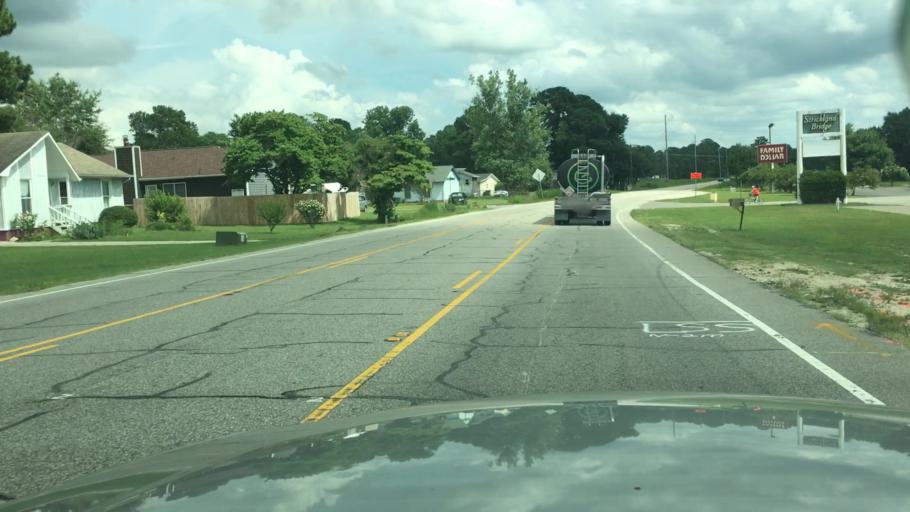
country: US
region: North Carolina
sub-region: Hoke County
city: Rockfish
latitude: 35.0155
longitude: -79.0073
